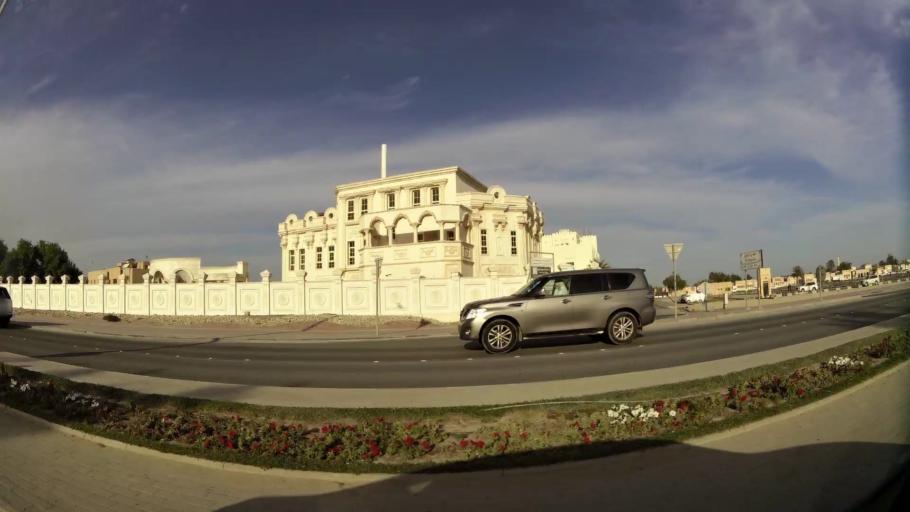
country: QA
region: Al Wakrah
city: Al Wakrah
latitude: 25.1740
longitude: 51.6064
